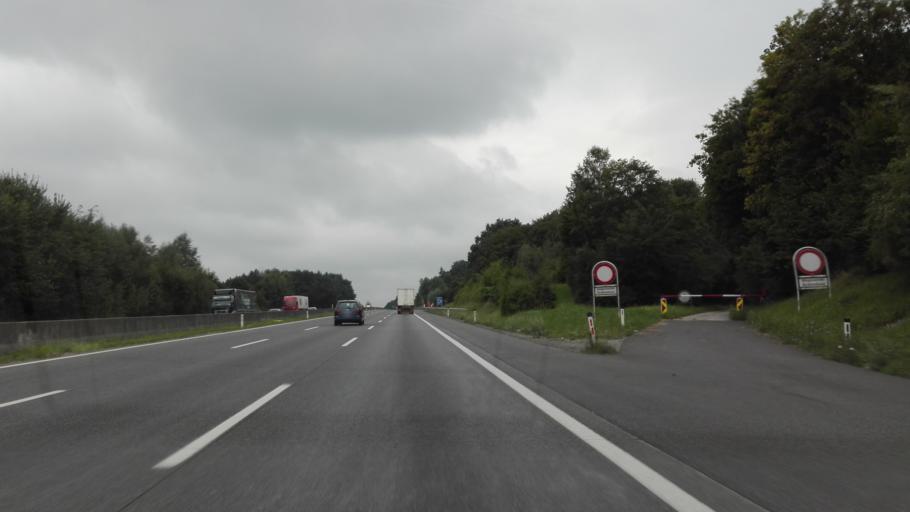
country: AT
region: Lower Austria
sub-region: Politischer Bezirk Melk
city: Blindenmarkt
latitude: 48.1377
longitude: 14.9684
